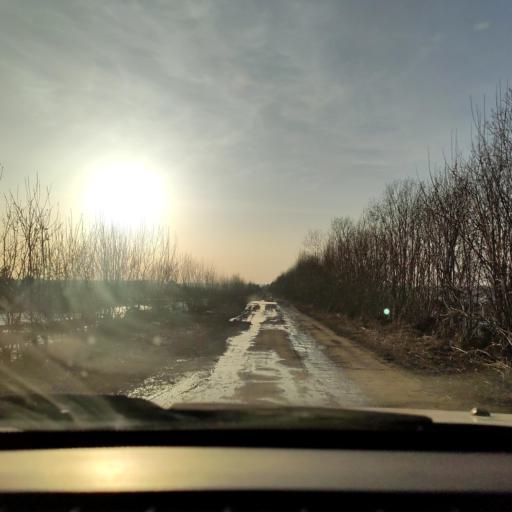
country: RU
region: Perm
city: Novyye Lyady
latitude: 58.1489
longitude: 56.4991
